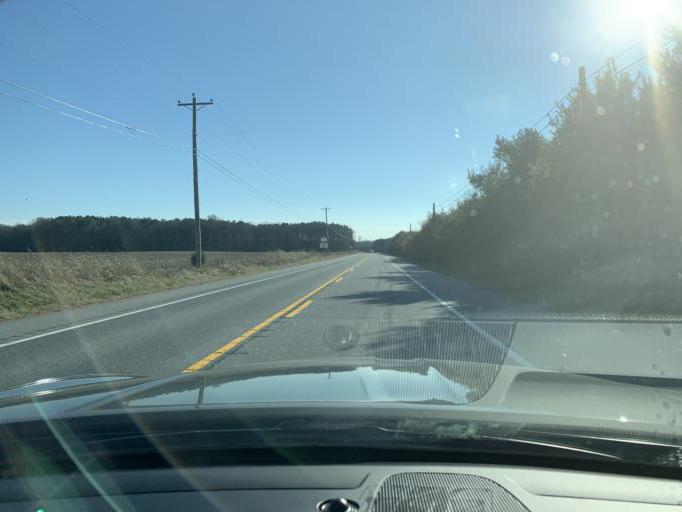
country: US
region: Maryland
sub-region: Queen Anne's County
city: Centreville
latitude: 39.0996
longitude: -76.0349
